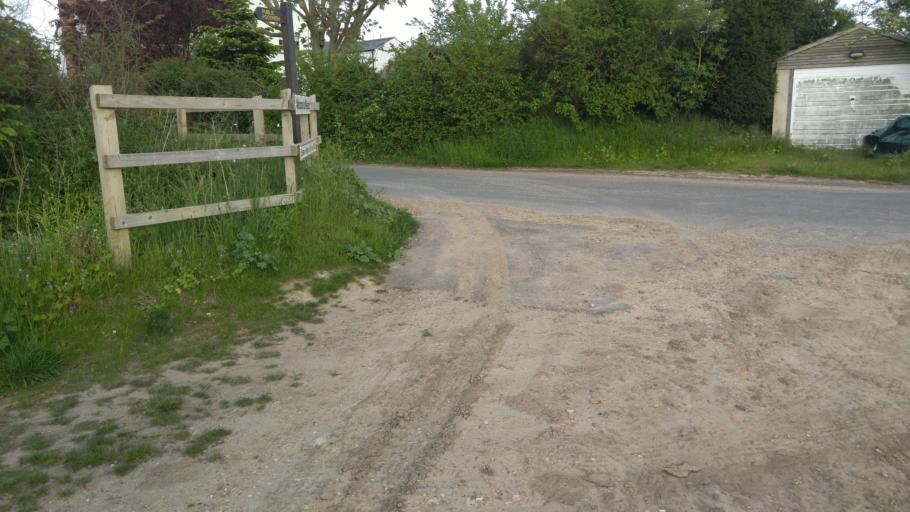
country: GB
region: England
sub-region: Essex
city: Tiptree
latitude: 51.8362
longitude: 0.7490
